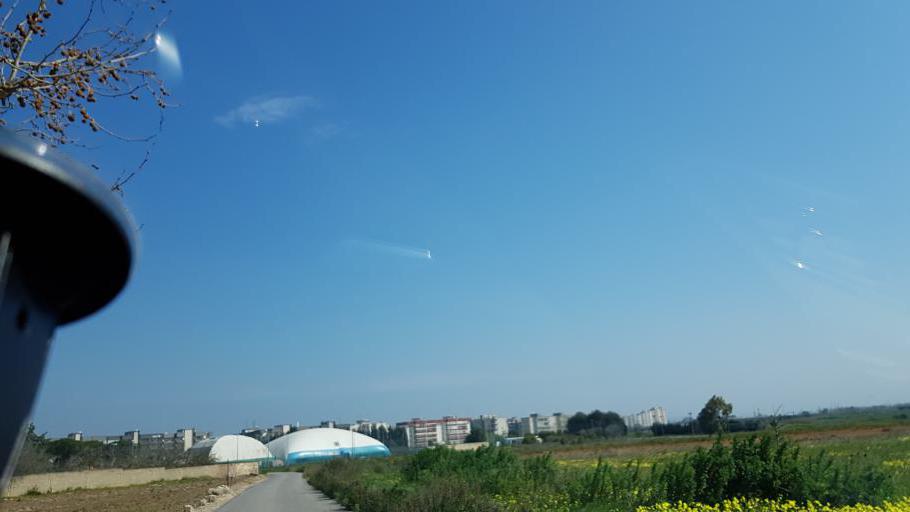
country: IT
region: Apulia
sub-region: Provincia di Brindisi
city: Brindisi
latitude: 40.6141
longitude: 17.9304
